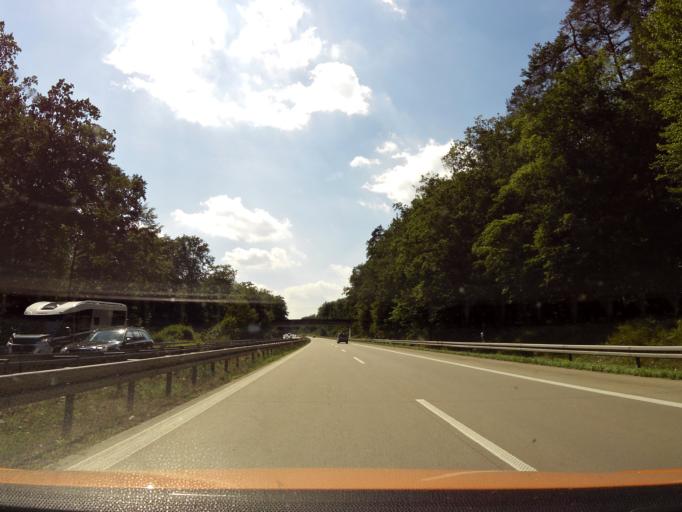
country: DE
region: Brandenburg
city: Gerswalde
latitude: 53.1125
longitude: 13.8615
